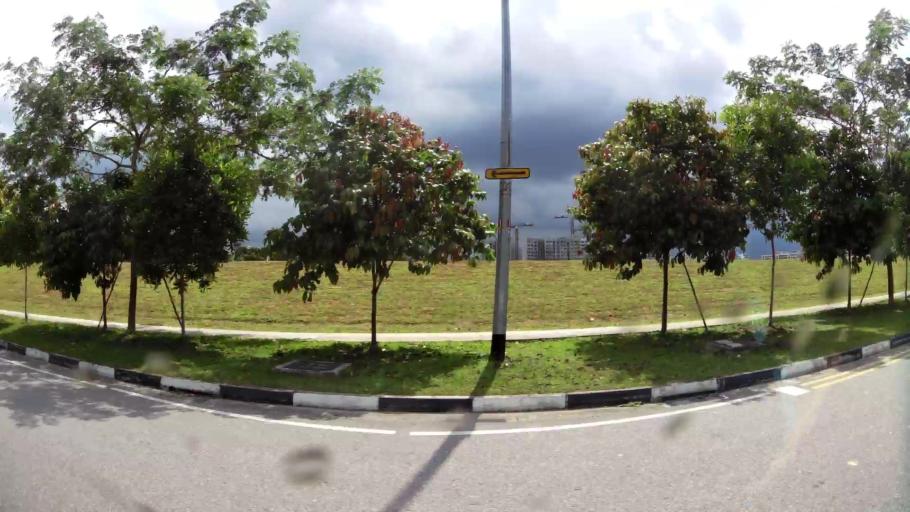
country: MY
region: Johor
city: Kampung Pasir Gudang Baru
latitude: 1.4279
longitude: 103.8543
